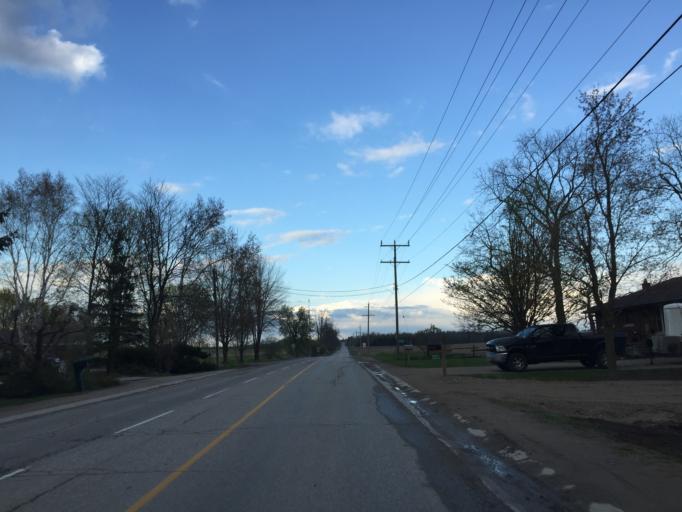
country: CA
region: Ontario
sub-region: Wellington County
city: Guelph
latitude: 43.5866
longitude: -80.2983
